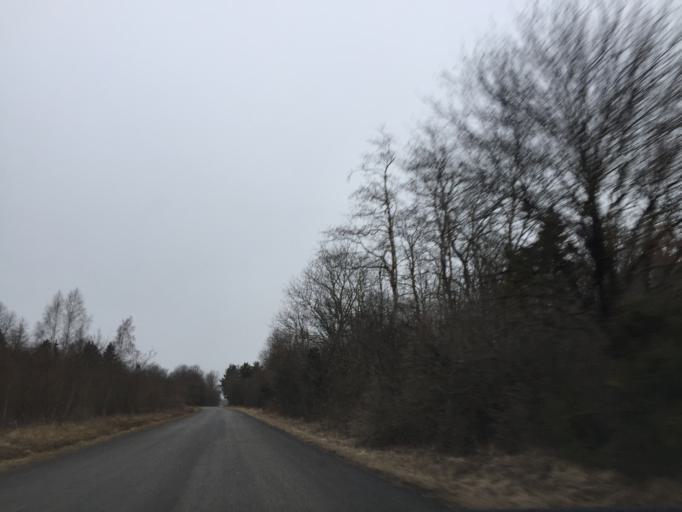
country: EE
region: Laeaene
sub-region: Lihula vald
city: Lihula
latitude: 58.6437
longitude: 23.6276
